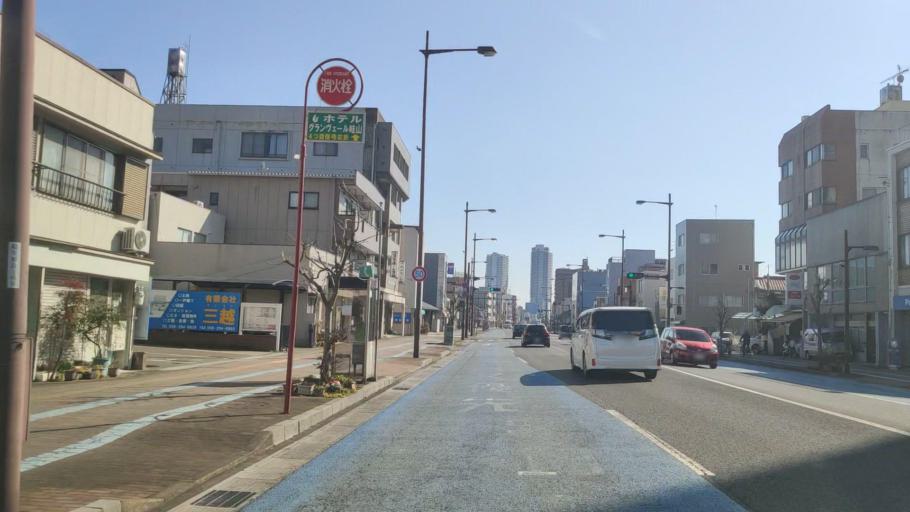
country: JP
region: Gifu
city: Gifu-shi
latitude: 35.4231
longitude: 136.7520
